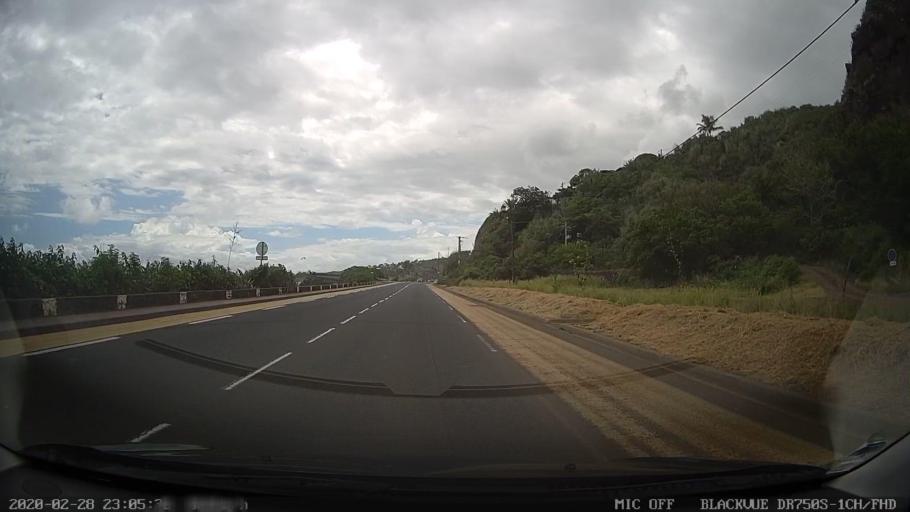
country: RE
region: Reunion
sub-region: Reunion
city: Saint-Leu
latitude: -21.1568
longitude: 55.2842
